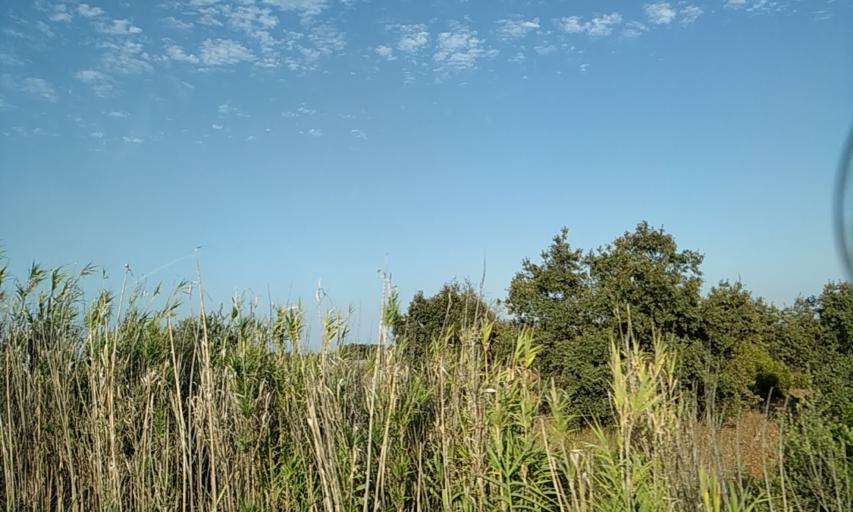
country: PT
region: Santarem
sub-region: Alcanena
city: Alcanena
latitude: 39.4127
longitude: -8.6377
